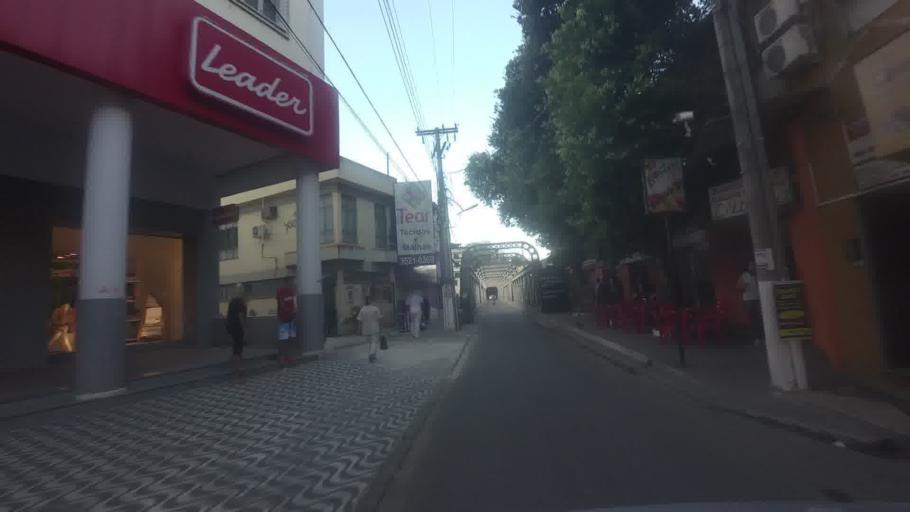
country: BR
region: Espirito Santo
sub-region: Cachoeiro De Itapemirim
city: Cachoeiro de Itapemirim
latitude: -20.8476
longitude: -41.1156
